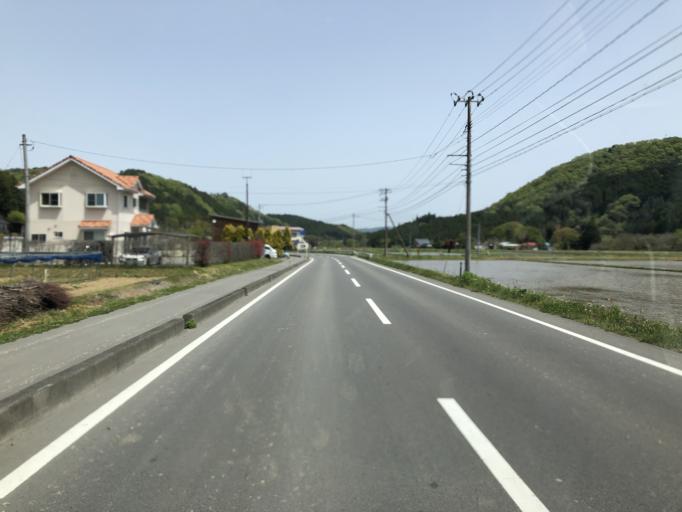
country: JP
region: Fukushima
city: Ishikawa
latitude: 37.0212
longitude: 140.3547
